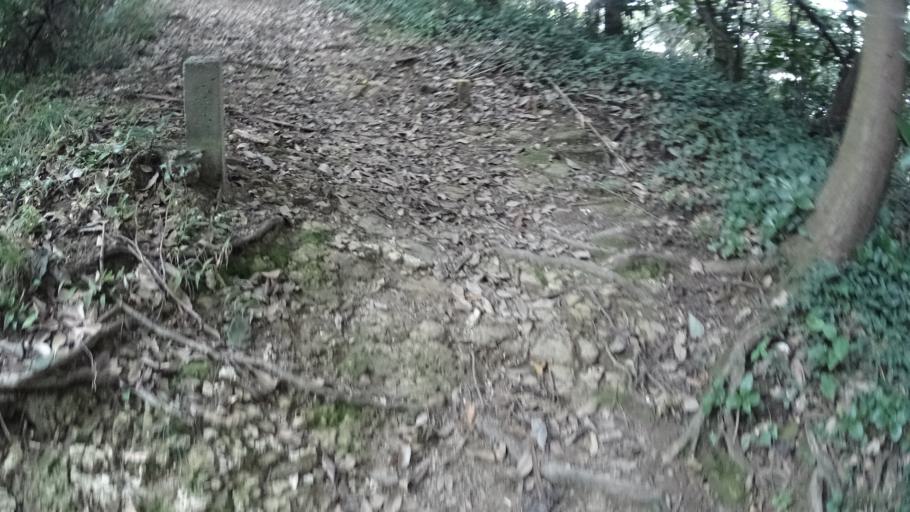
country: JP
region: Kanagawa
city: Zushi
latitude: 35.2911
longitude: 139.6220
